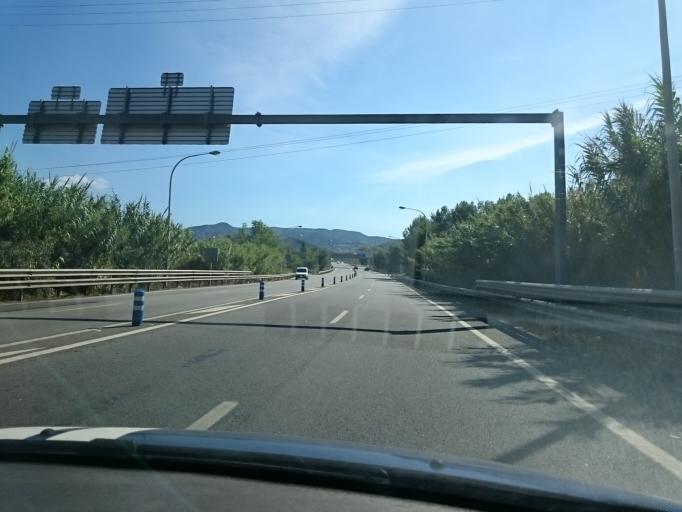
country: ES
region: Catalonia
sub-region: Provincia de Barcelona
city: Mollet del Valles
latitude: 41.5281
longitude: 2.2059
